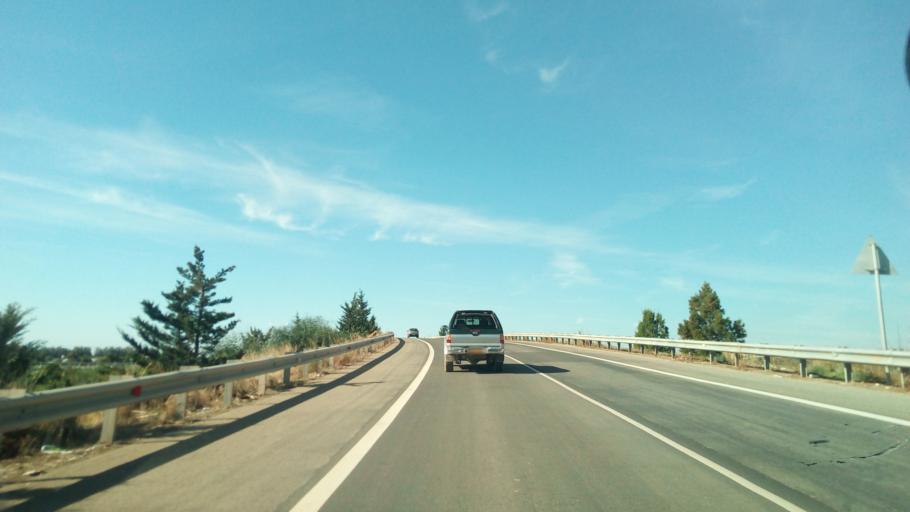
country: CY
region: Pafos
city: Paphos
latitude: 34.7213
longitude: 32.5333
